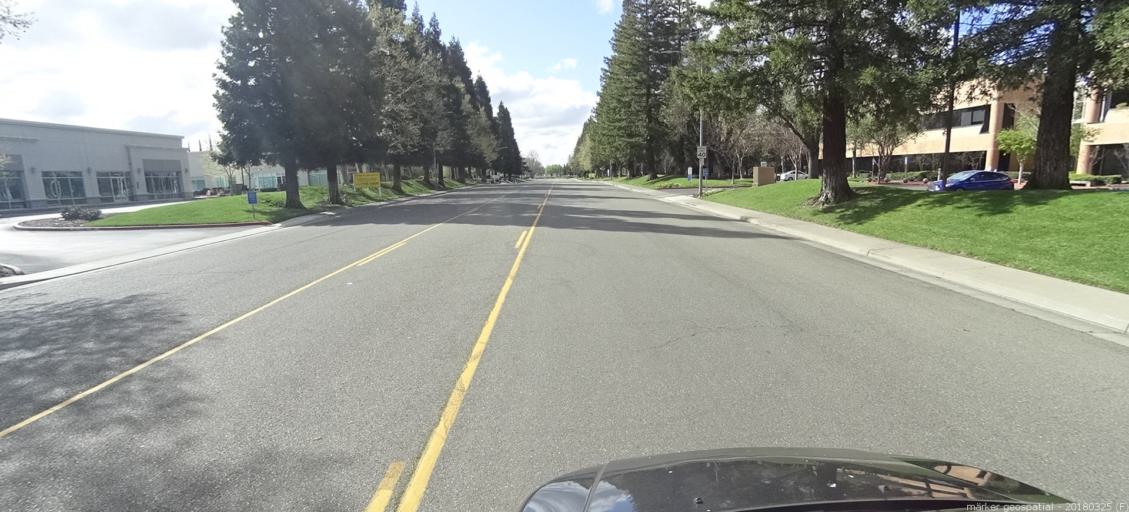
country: US
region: California
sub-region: Sacramento County
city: Sacramento
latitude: 38.6431
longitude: -121.4915
